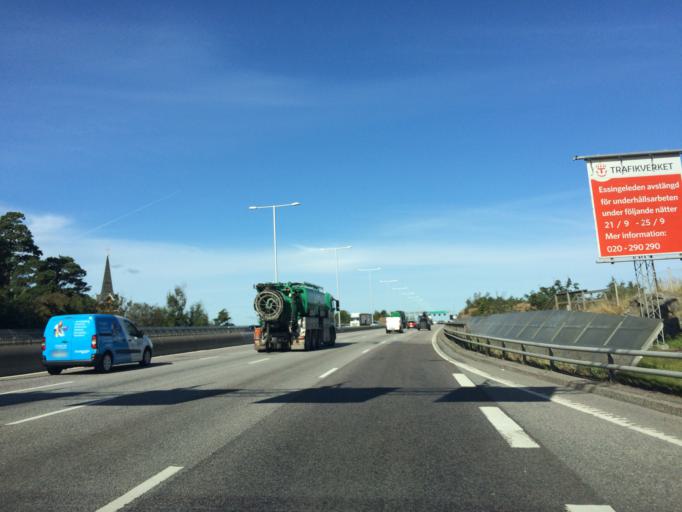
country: SE
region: Stockholm
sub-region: Stockholms Kommun
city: Arsta
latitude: 59.3092
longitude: 18.0086
